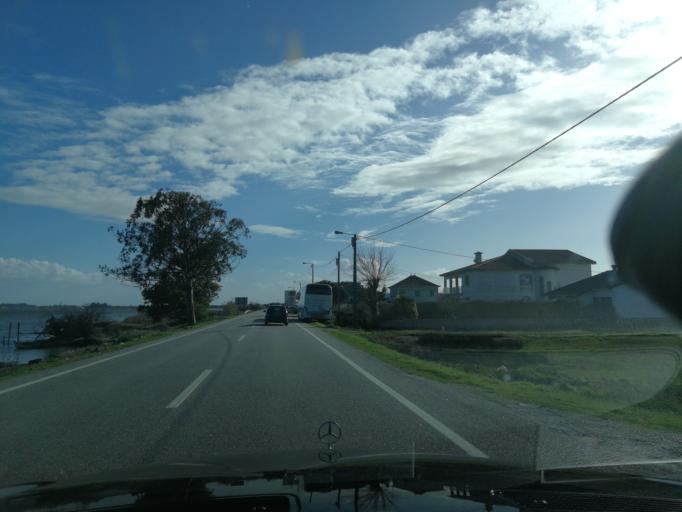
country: PT
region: Aveiro
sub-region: Estarreja
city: Pardilho
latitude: 40.7981
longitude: -8.6740
